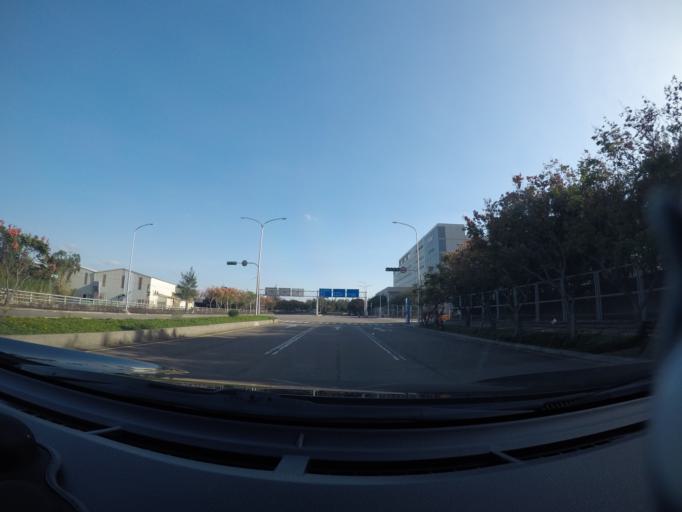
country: TW
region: Taiwan
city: Taoyuan City
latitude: 25.0963
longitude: 121.2567
